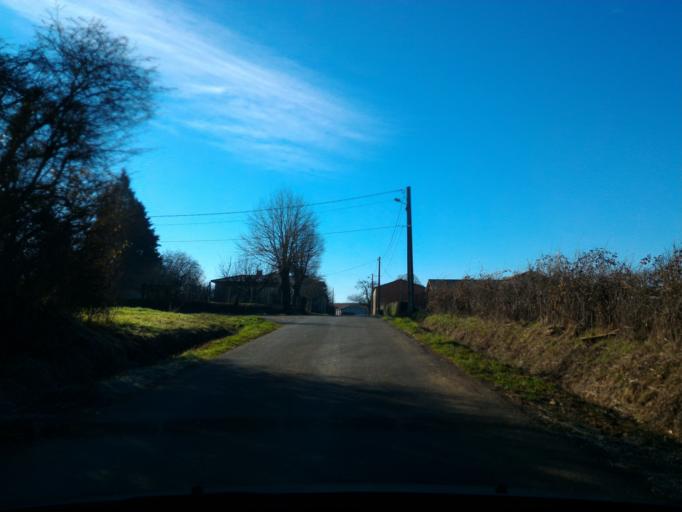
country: FR
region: Poitou-Charentes
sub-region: Departement de la Charente
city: Champagne-Mouton
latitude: 45.9717
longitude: 0.3942
